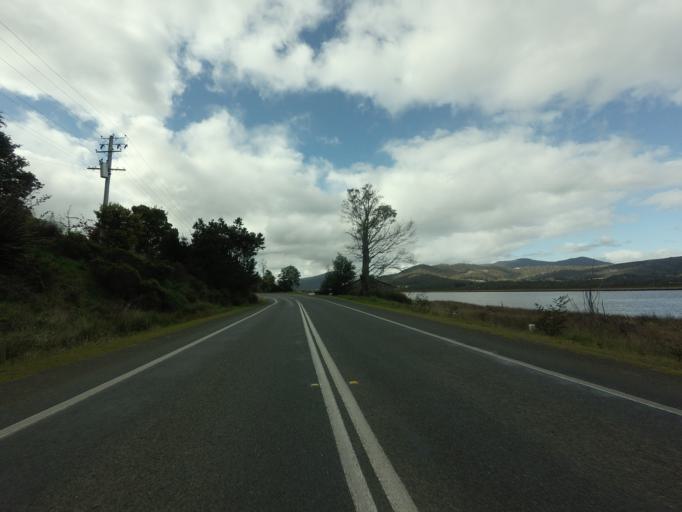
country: AU
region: Tasmania
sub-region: Huon Valley
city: Franklin
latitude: -43.1027
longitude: 147.0025
